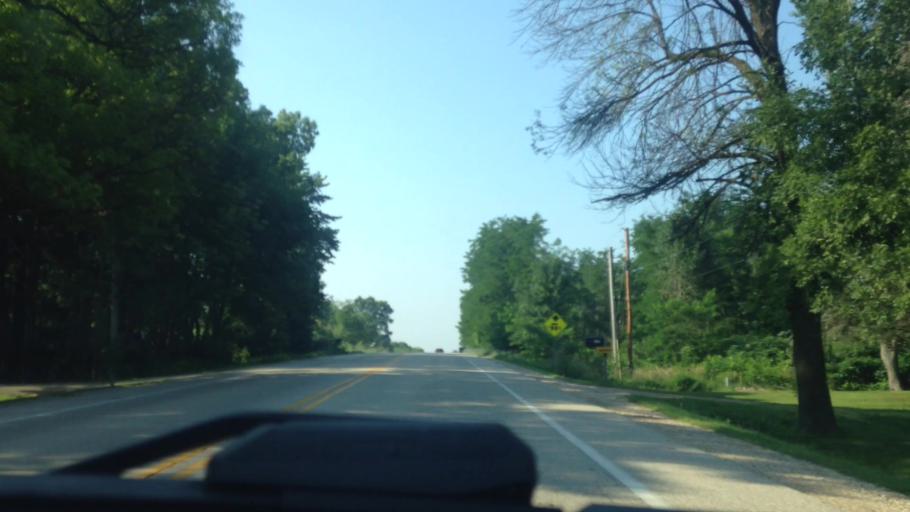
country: US
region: Wisconsin
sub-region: Washington County
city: Slinger
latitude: 43.3043
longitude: -88.2608
